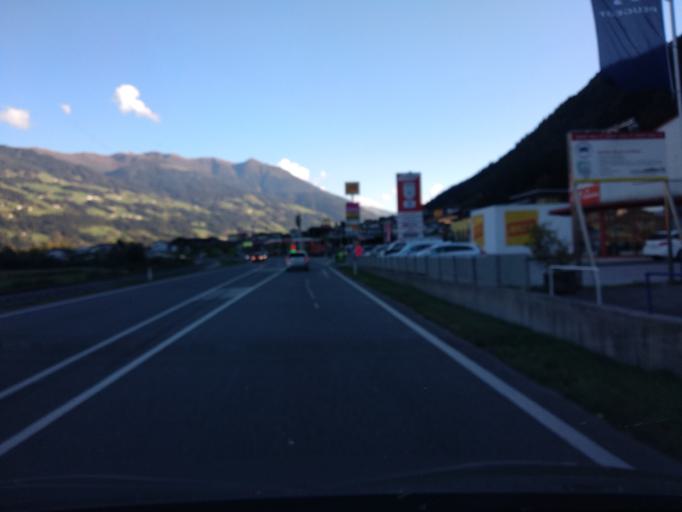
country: AT
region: Tyrol
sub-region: Politischer Bezirk Schwaz
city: Schlitters
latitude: 47.3827
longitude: 11.8325
